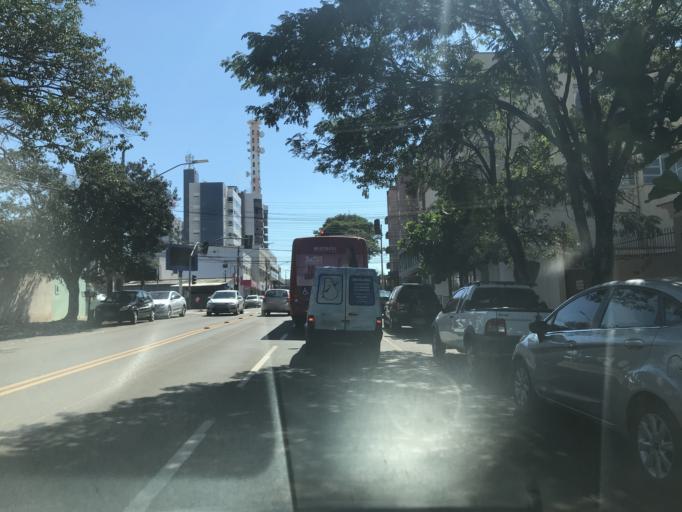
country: BR
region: Parana
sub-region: Toledo
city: Toledo
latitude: -24.7347
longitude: -53.7421
